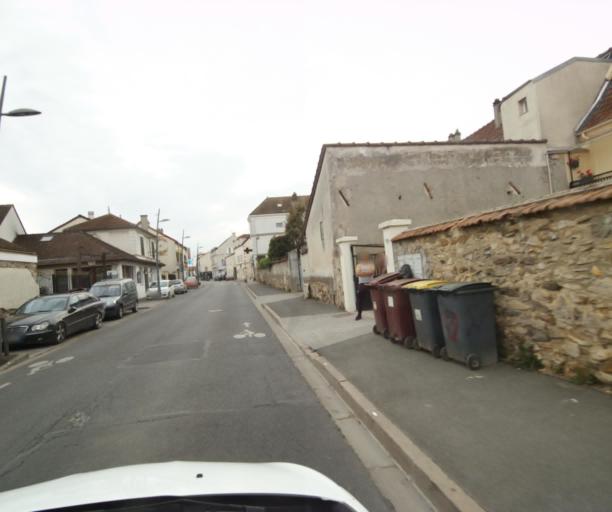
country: FR
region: Ile-de-France
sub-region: Departement de Seine-et-Marne
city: Torcy
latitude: 48.8509
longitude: 2.6556
